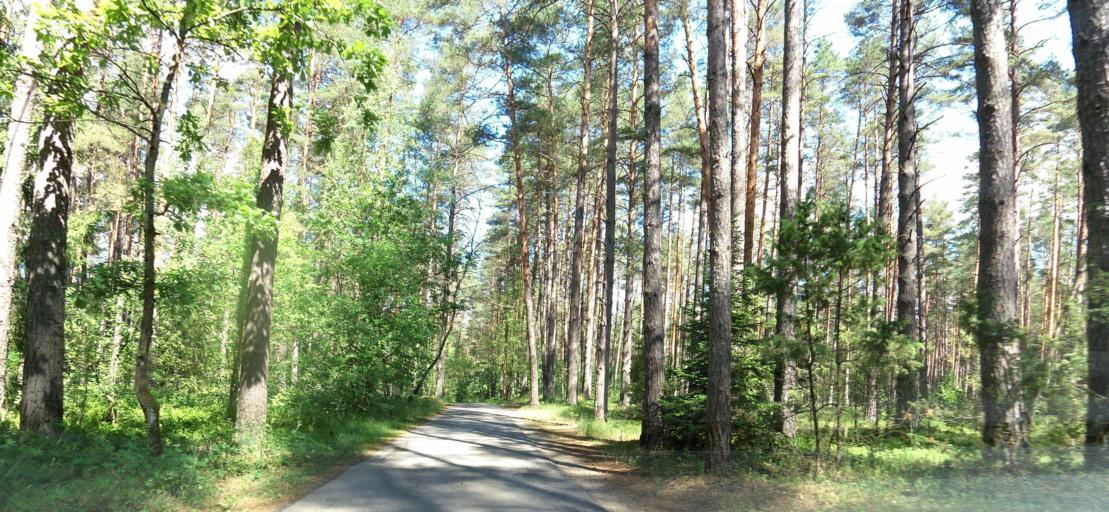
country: LT
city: Nemencine
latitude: 54.8112
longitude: 25.3931
